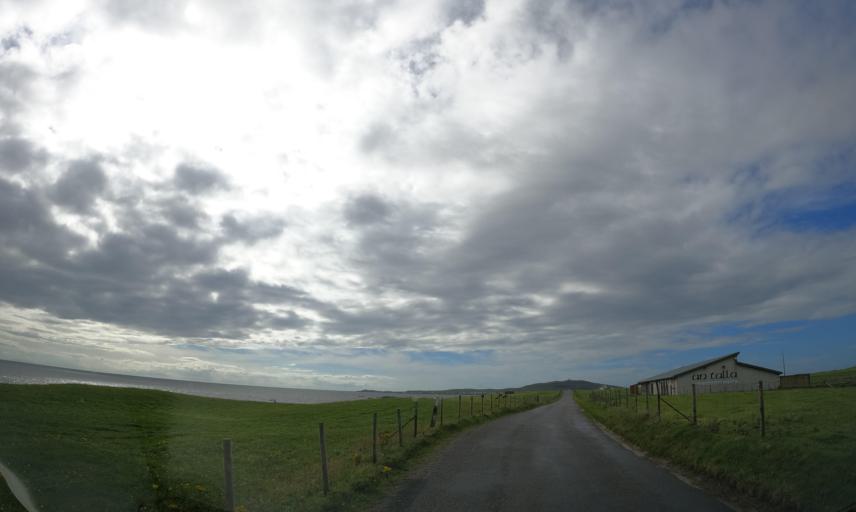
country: GB
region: Scotland
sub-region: Eilean Siar
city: Barra
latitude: 56.4843
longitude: -6.8805
